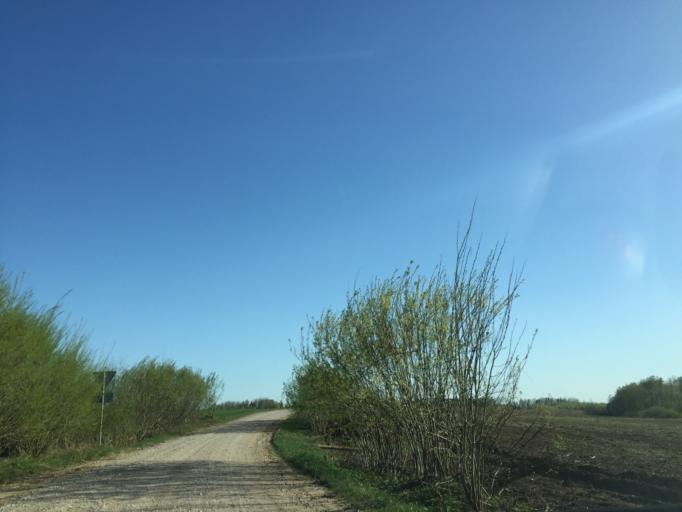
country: LV
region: Ergli
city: Ergli
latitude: 56.9016
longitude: 25.4965
